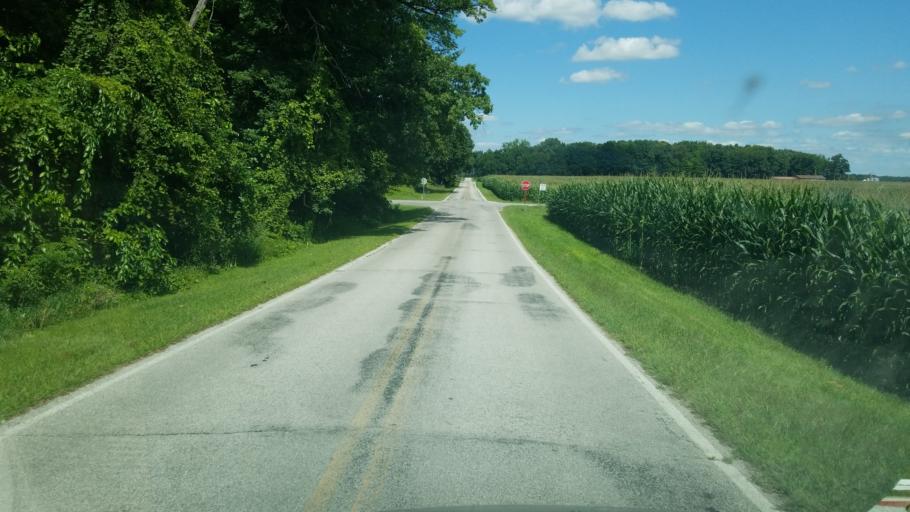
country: US
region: Ohio
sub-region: Fulton County
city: Delta
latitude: 41.6278
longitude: -84.0153
